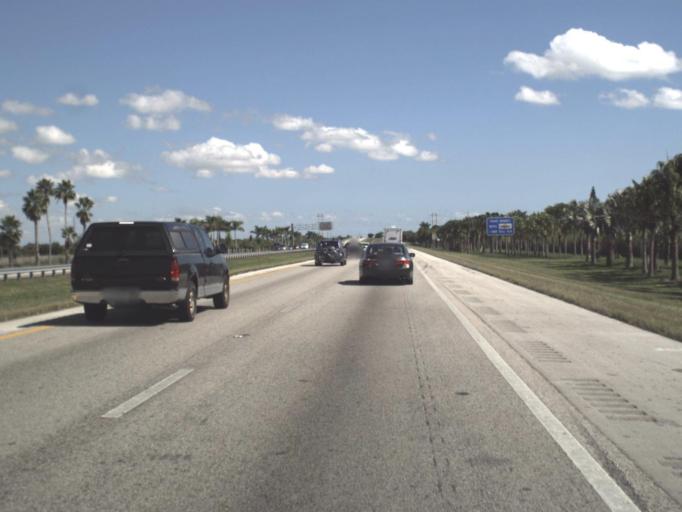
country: US
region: Florida
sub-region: Miami-Dade County
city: Homestead
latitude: 25.4577
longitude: -80.4690
